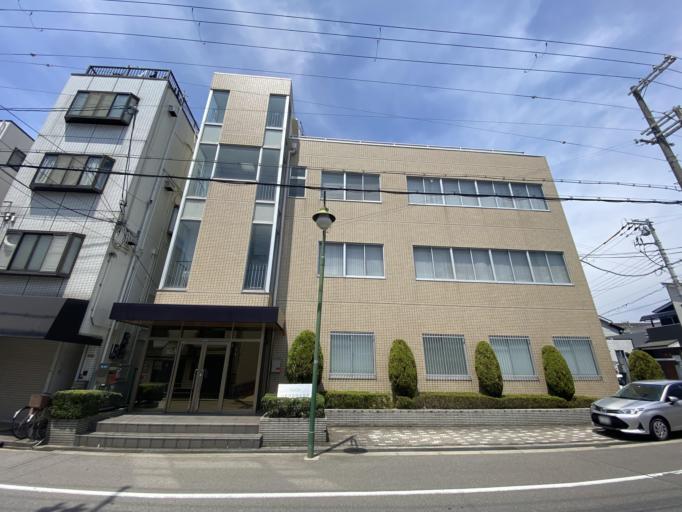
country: JP
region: Hyogo
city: Amagasaki
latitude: 34.7147
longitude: 135.4545
